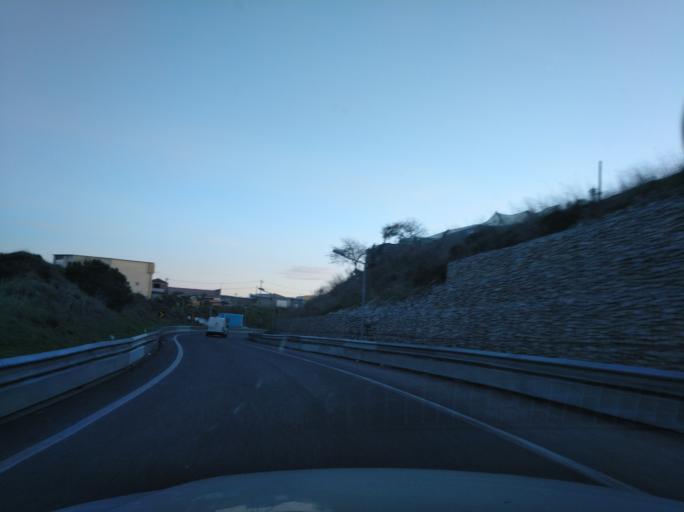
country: PT
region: Lisbon
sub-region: Loures
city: Camarate
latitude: 38.7963
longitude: -9.1430
